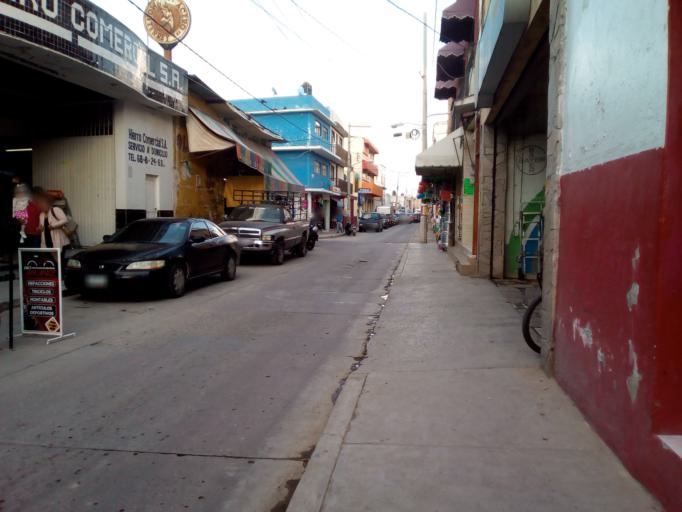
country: MX
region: Guerrero
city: San Luis de la Paz
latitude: 21.2971
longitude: -100.5228
